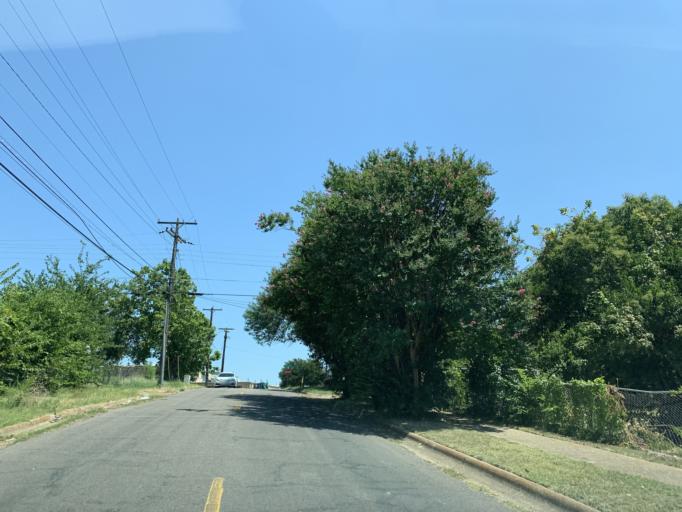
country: US
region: Texas
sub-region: Dallas County
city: Hutchins
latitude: 32.6792
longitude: -96.7641
